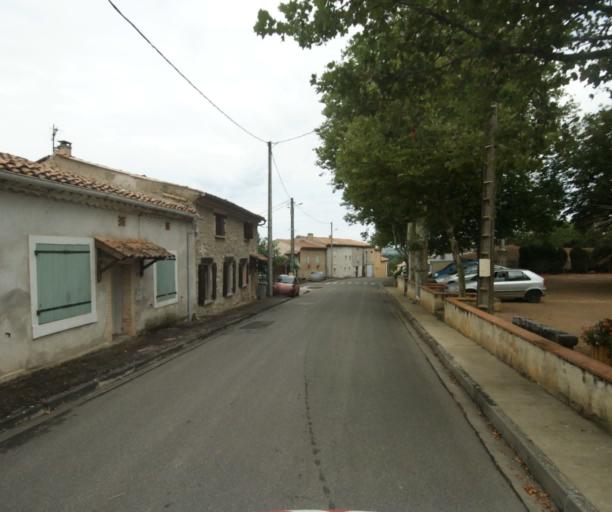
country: FR
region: Midi-Pyrenees
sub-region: Departement de la Haute-Garonne
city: Revel
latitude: 43.4358
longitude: 1.9681
